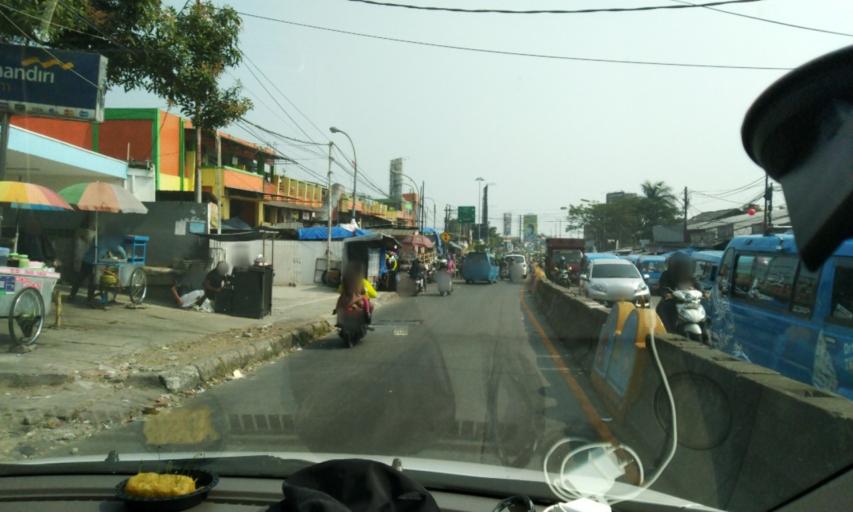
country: ID
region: West Java
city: Caringin
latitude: -6.6569
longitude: 106.8482
